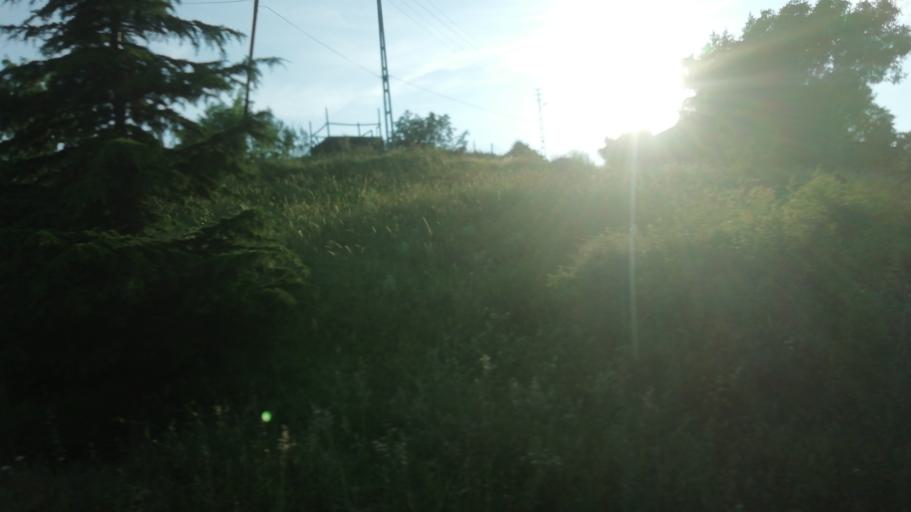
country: TR
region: Karabuk
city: Karabuk
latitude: 41.1280
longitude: 32.6217
